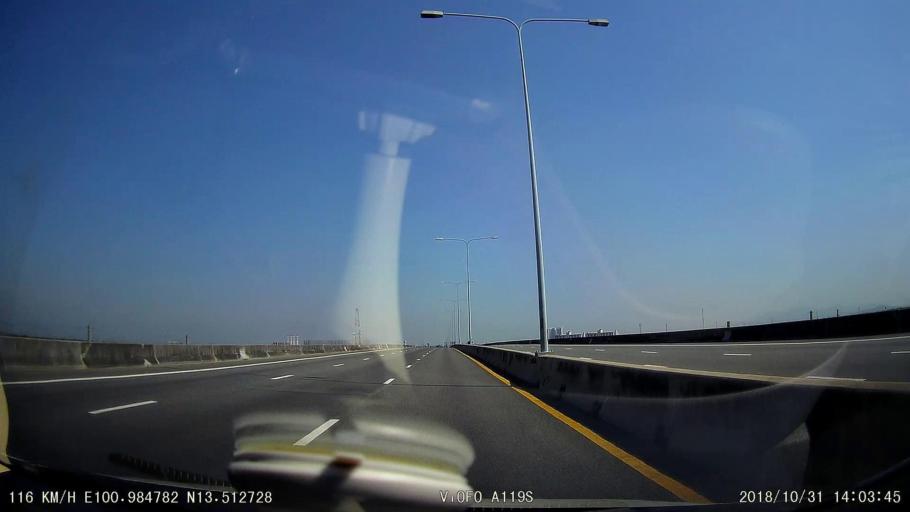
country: TH
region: Chachoengsao
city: Bang Pakong
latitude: 13.5126
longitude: 100.9850
